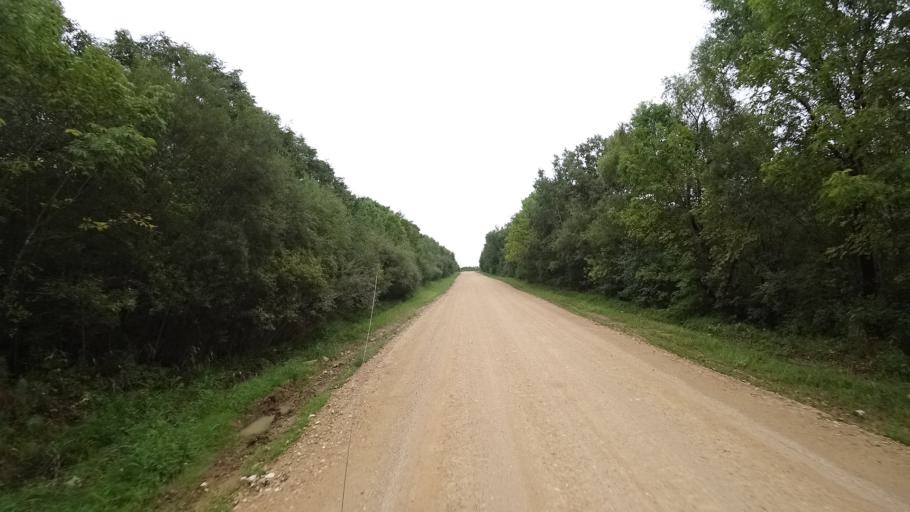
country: RU
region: Primorskiy
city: Monastyrishche
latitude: 44.0837
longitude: 132.5953
